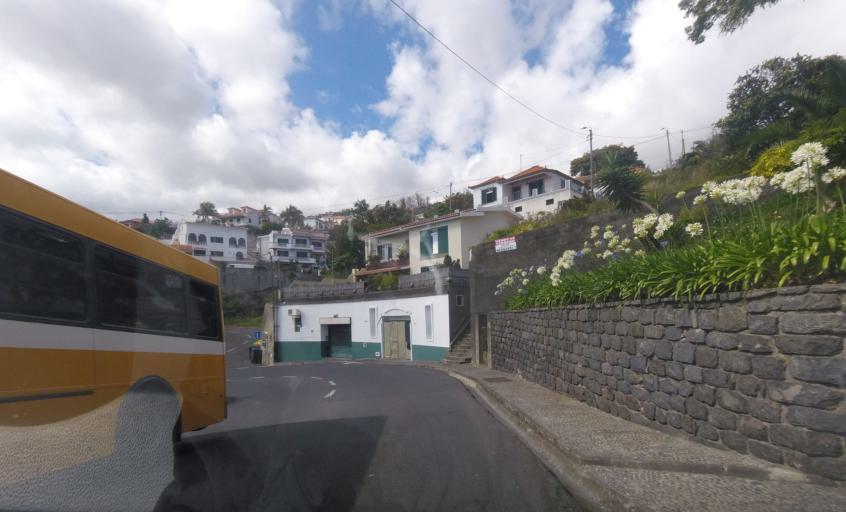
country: PT
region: Madeira
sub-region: Funchal
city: Nossa Senhora do Monte
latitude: 32.6581
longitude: -16.8901
